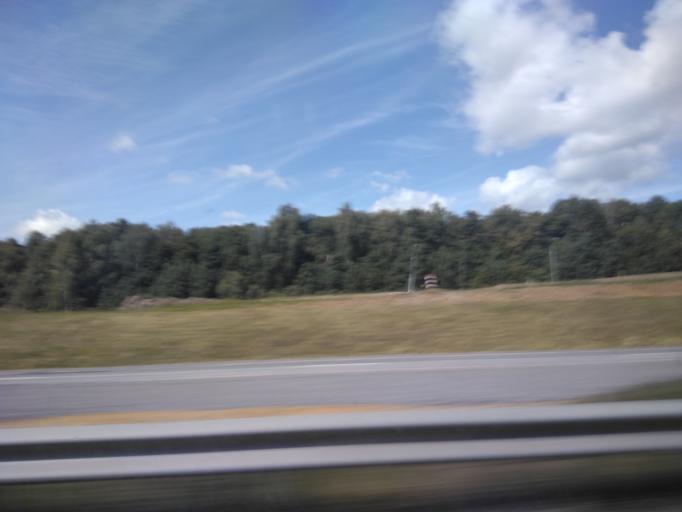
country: RU
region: Tula
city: Zaokskiy
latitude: 54.5923
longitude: 37.5014
